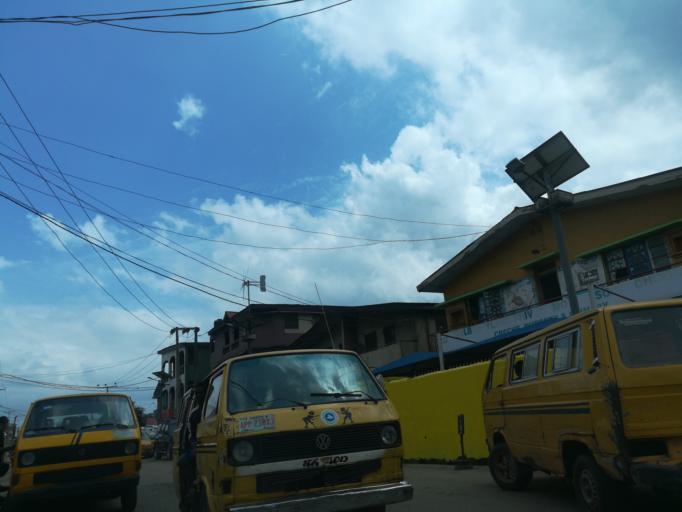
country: NG
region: Lagos
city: Somolu
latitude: 6.5331
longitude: 3.3648
